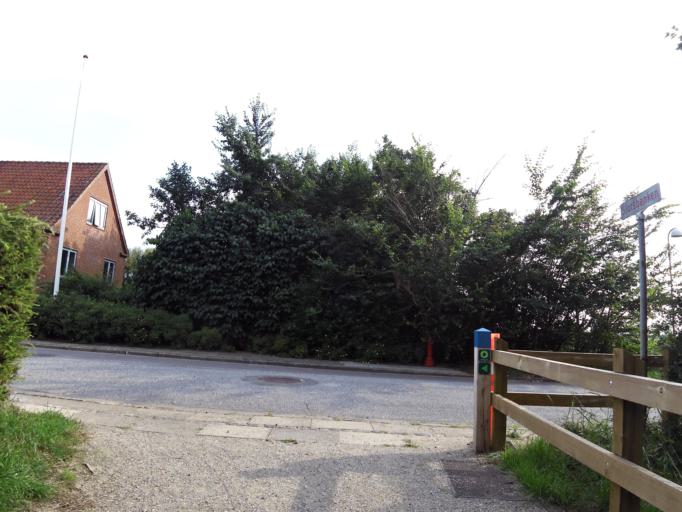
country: DK
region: South Denmark
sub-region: Esbjerg Kommune
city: Ribe
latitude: 55.3276
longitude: 8.7537
